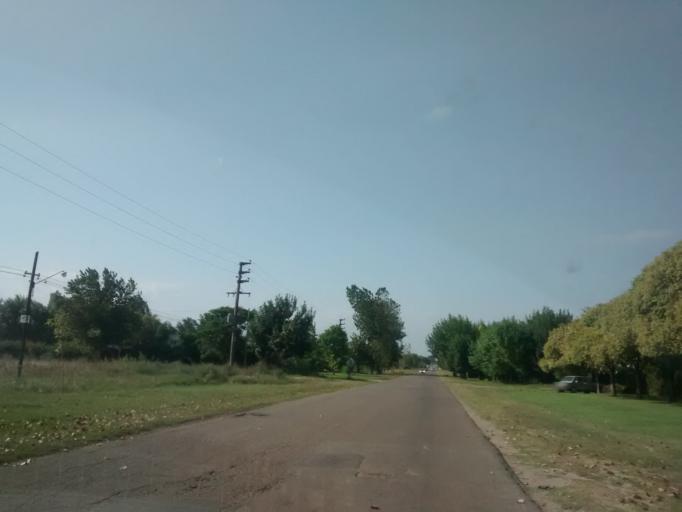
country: AR
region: Buenos Aires
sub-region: Partido de La Plata
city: La Plata
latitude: -35.0024
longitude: -57.8987
